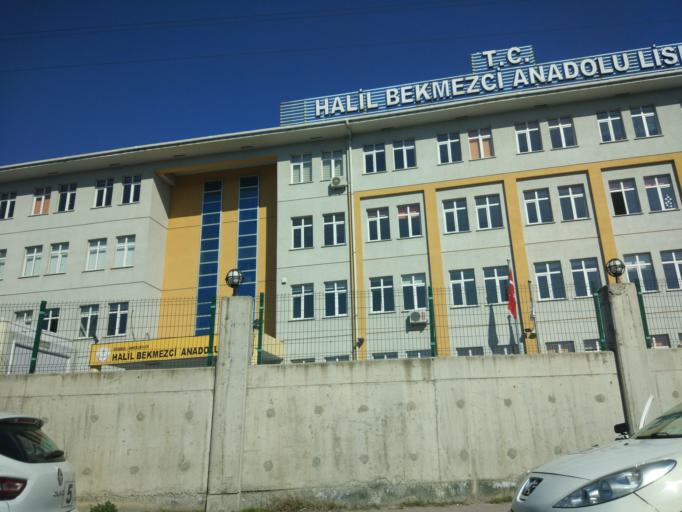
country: TR
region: Istanbul
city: Mahmutbey
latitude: 41.0186
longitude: 28.8132
